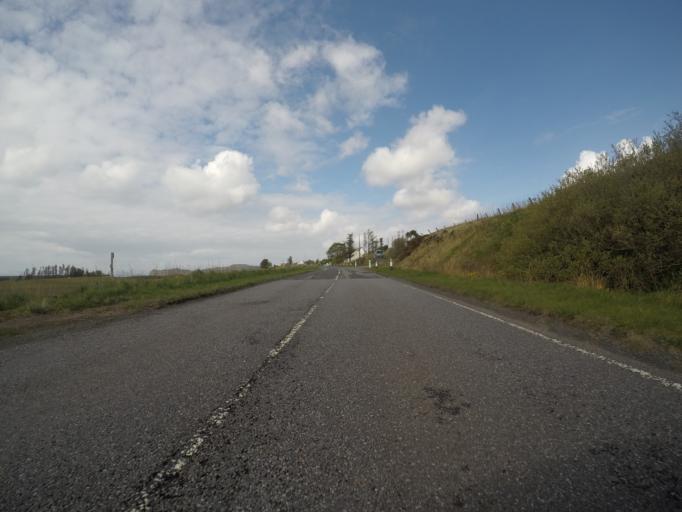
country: GB
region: Scotland
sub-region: Highland
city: Portree
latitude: 57.5635
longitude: -6.3644
